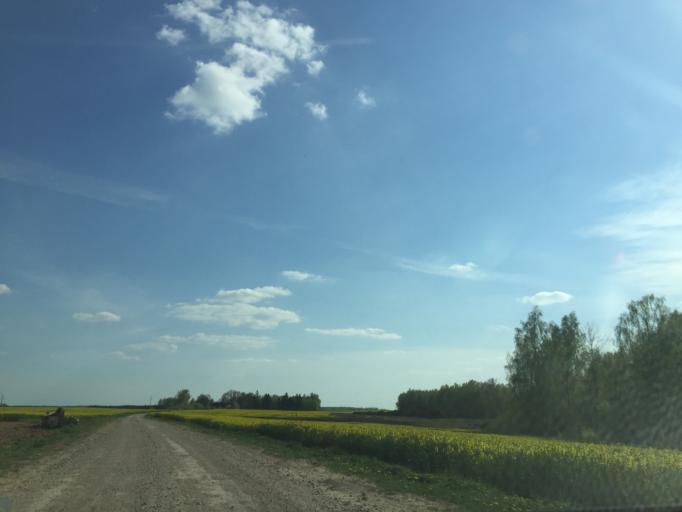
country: LV
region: Lecava
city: Iecava
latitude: 56.4977
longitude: 24.3178
